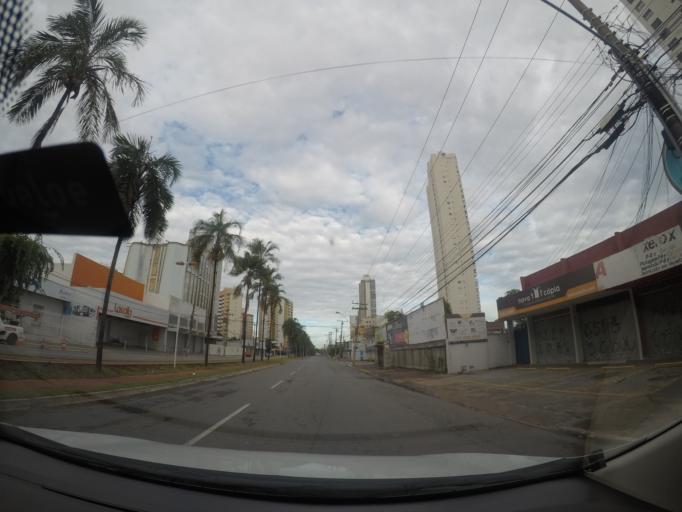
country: BR
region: Goias
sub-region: Goiania
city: Goiania
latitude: -16.6867
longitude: -49.2728
